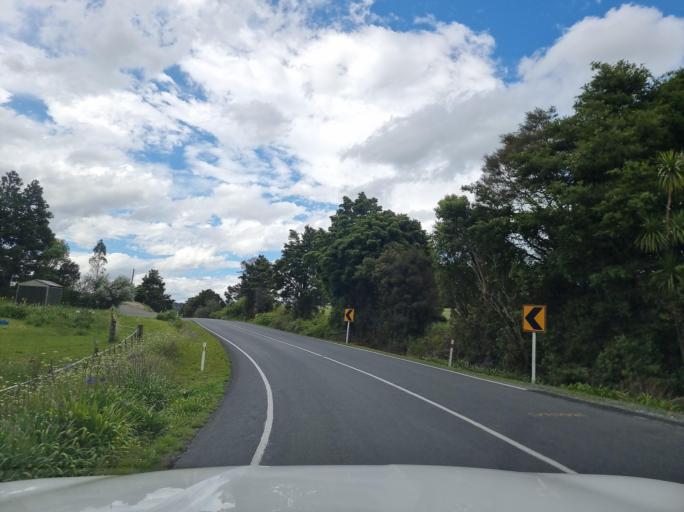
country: NZ
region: Northland
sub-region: Whangarei
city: Maungatapere
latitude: -35.8530
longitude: 174.2622
